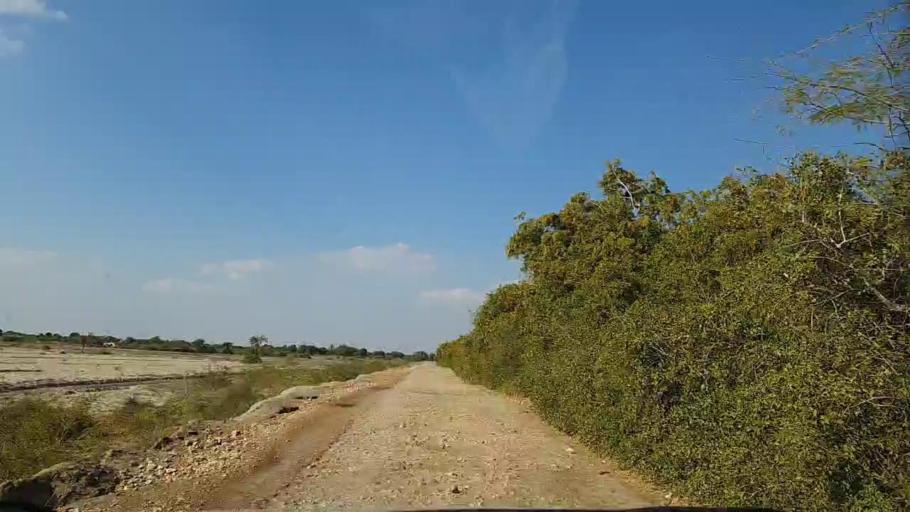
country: PK
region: Sindh
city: Pithoro
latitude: 25.6234
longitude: 69.3538
